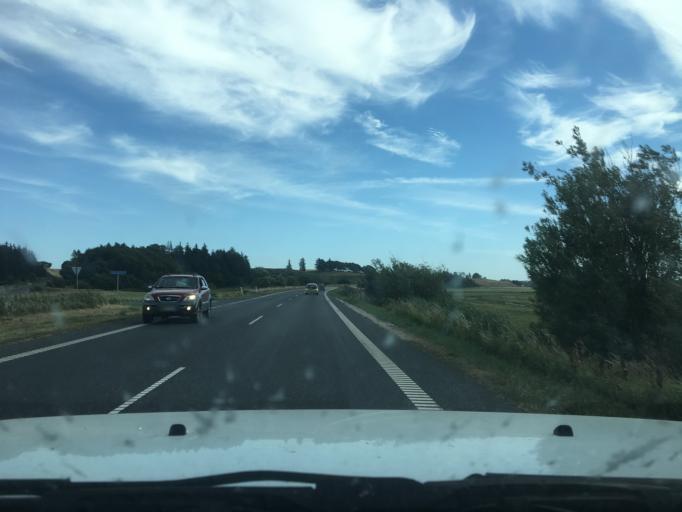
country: DK
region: Central Jutland
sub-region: Viborg Kommune
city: Viborg
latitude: 56.5704
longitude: 9.3821
